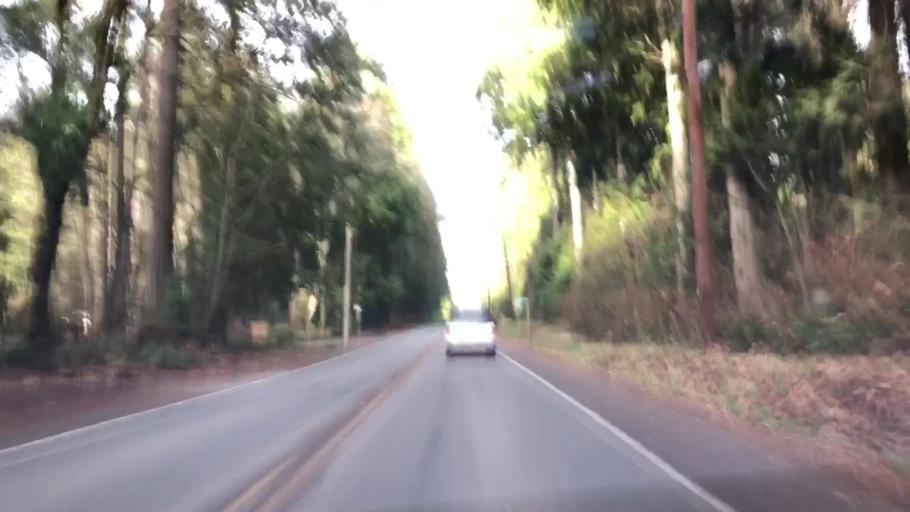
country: US
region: Washington
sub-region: Kitsap County
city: Indianola
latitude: 47.7639
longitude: -122.5524
